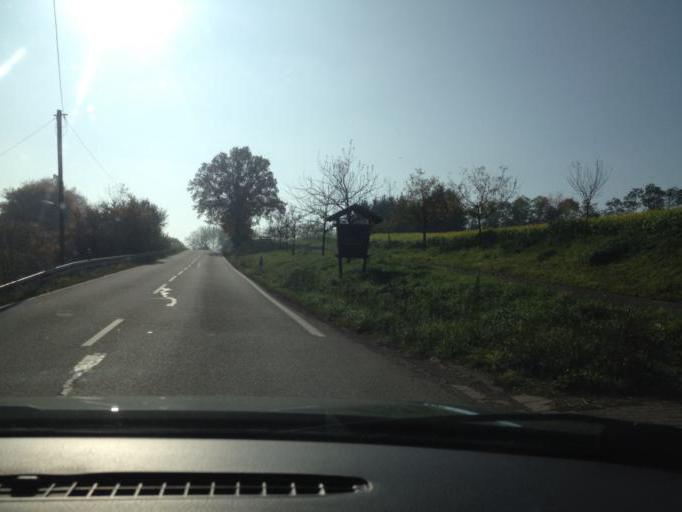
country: DE
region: Saarland
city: Namborn
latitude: 49.5066
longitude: 7.1660
